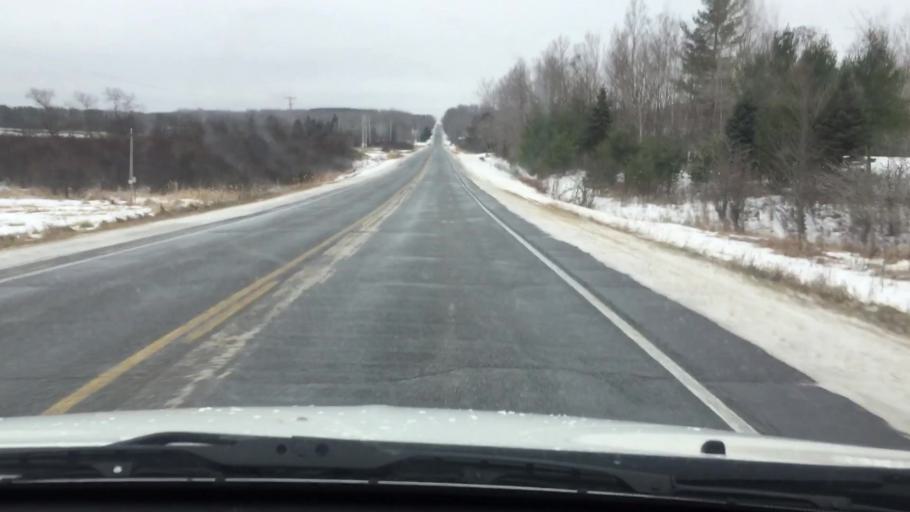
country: US
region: Michigan
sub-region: Wexford County
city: Cadillac
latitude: 44.1077
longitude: -85.4442
